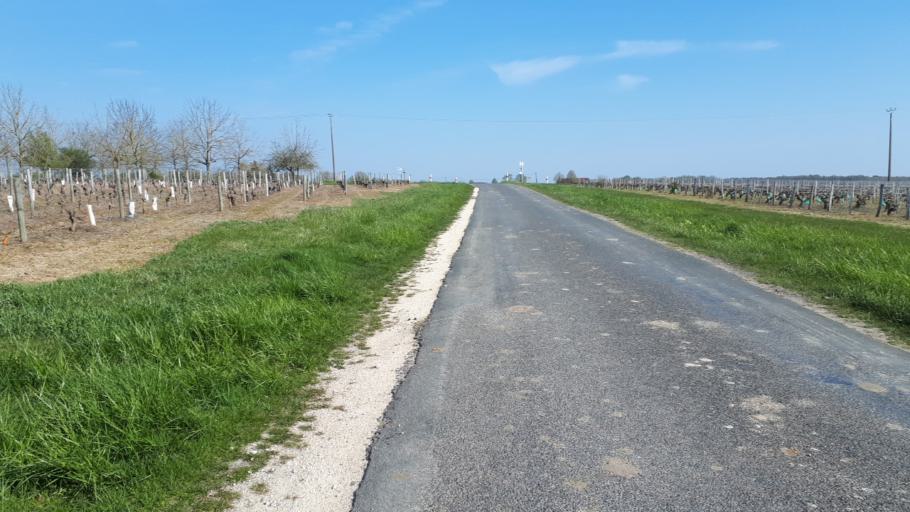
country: FR
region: Centre
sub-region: Departement du Loir-et-Cher
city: Contres
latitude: 47.3870
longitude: 1.3860
